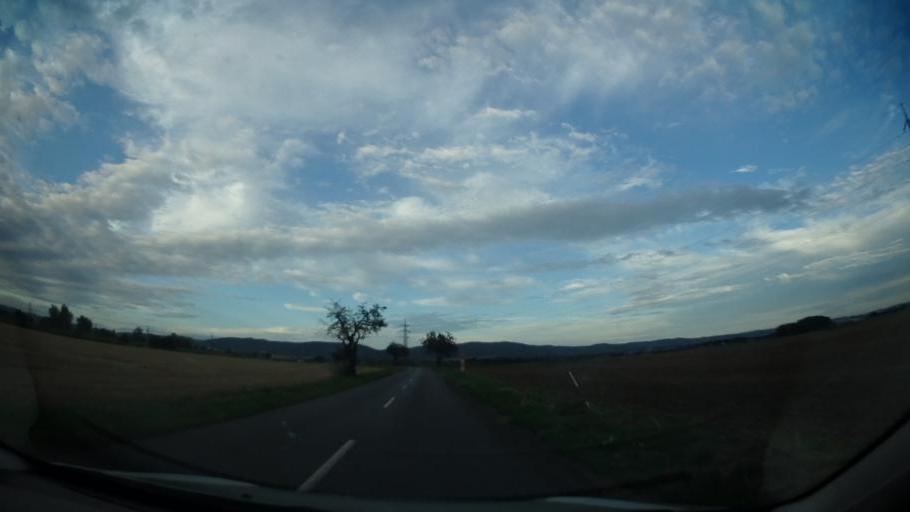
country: CZ
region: Olomoucky
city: Ujezd
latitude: 49.7752
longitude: 17.1579
